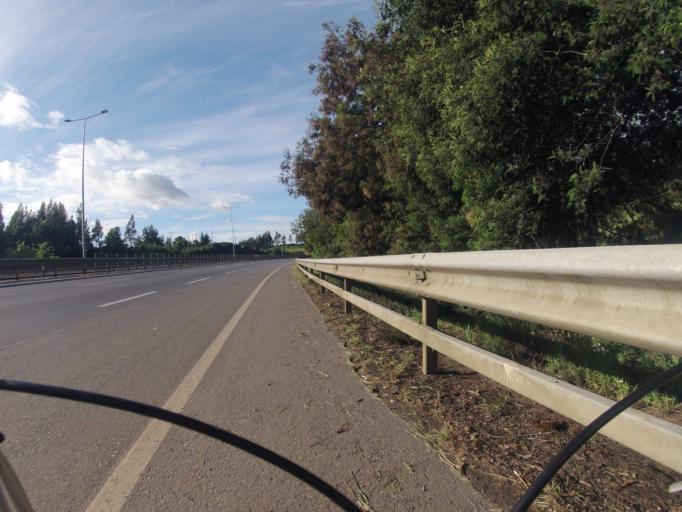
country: CL
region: Araucania
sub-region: Provincia de Cautin
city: Temuco
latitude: -38.8061
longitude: -72.6268
